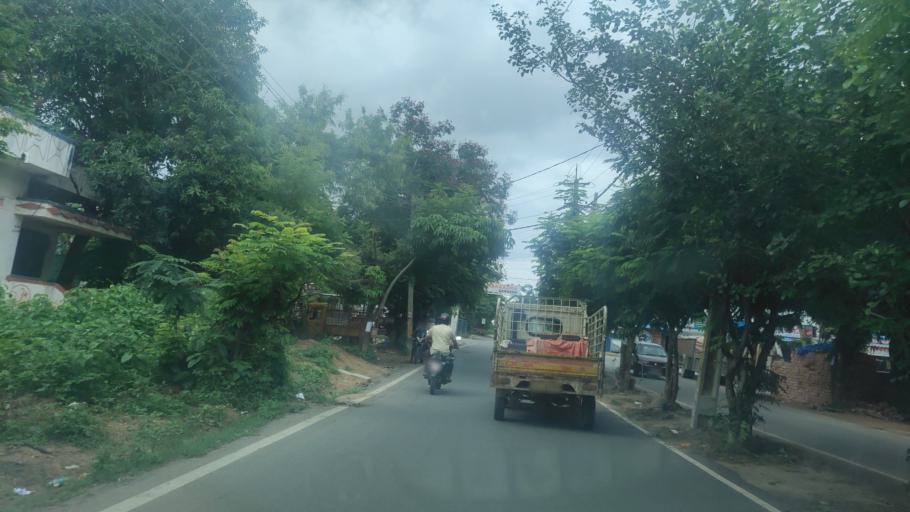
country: IN
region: Telangana
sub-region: Medak
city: Serilingampalle
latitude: 17.5071
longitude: 78.3536
